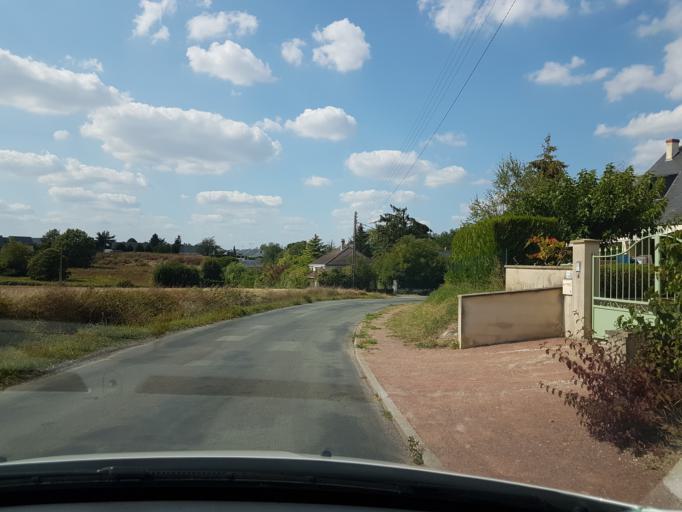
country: FR
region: Centre
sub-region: Departement d'Indre-et-Loire
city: Larcay
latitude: 47.3636
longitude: 0.7806
